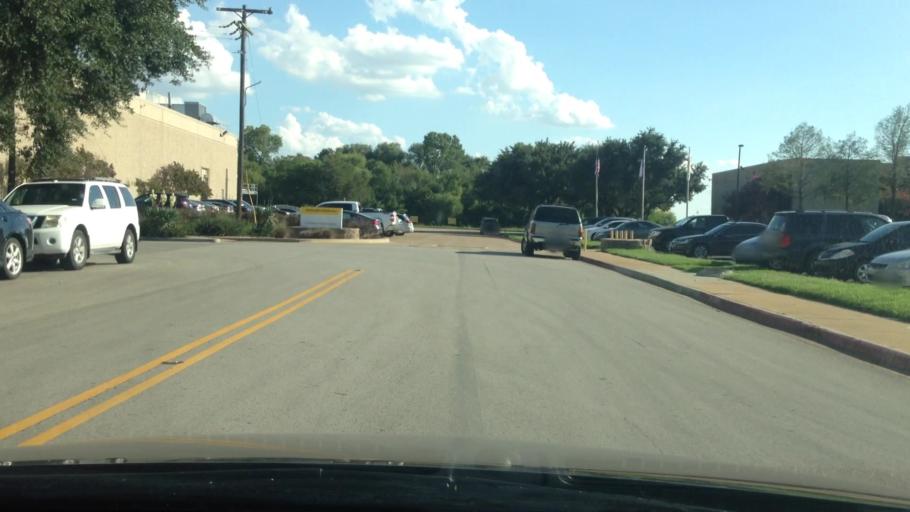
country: US
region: Texas
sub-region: Dallas County
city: Farmers Branch
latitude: 32.9173
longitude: -96.9054
